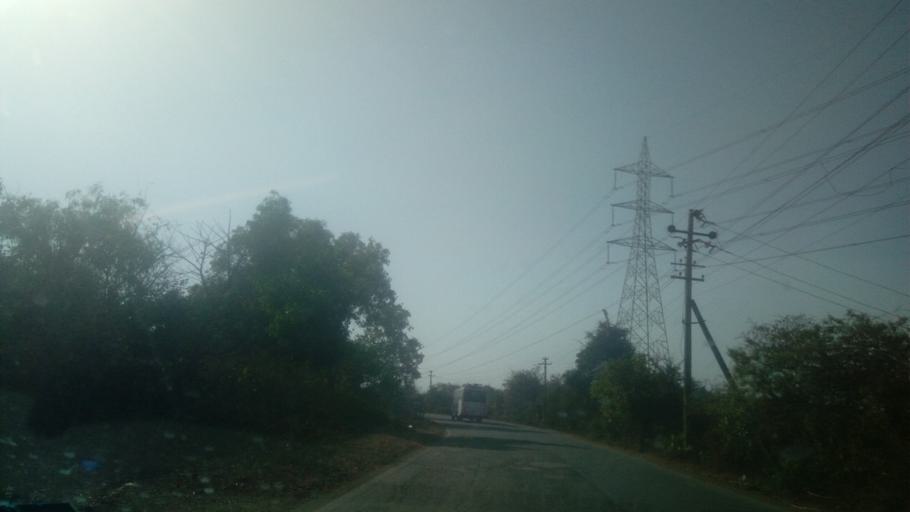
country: IN
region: Goa
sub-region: North Goa
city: Navelim
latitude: 15.5297
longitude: 73.9913
